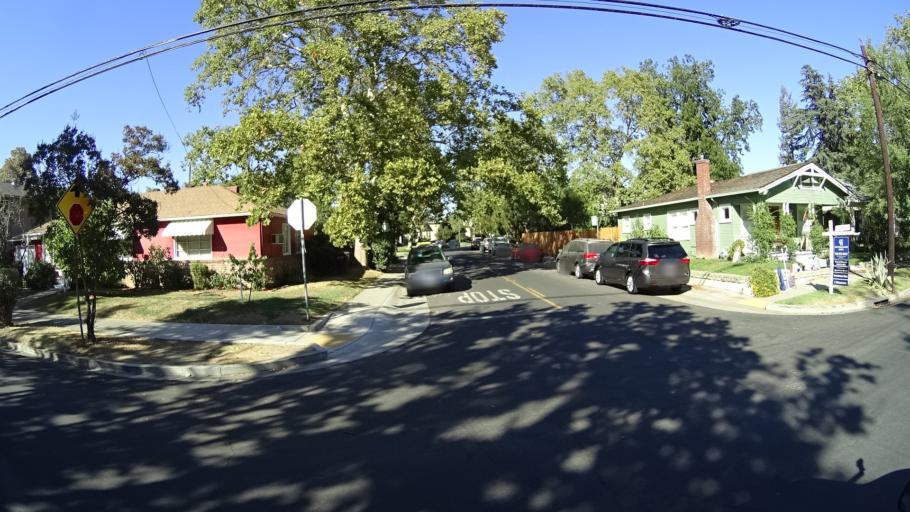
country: US
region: California
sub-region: Sacramento County
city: Sacramento
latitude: 38.5544
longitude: -121.4792
